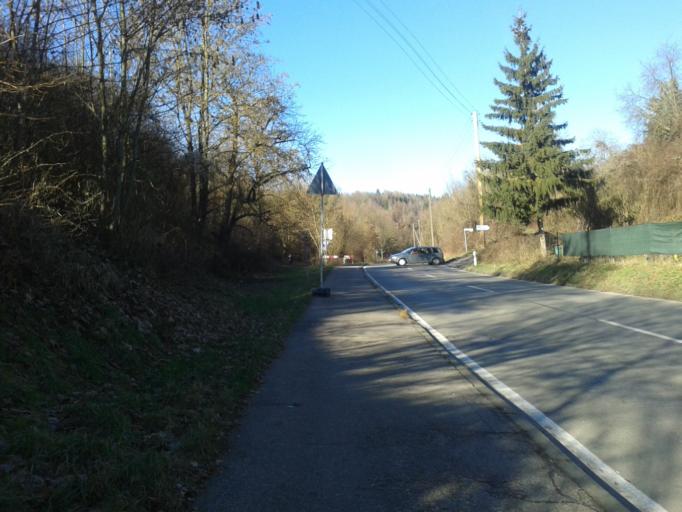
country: DE
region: Baden-Wuerttemberg
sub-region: Tuebingen Region
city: Ulm
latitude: 48.4119
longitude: 9.9706
